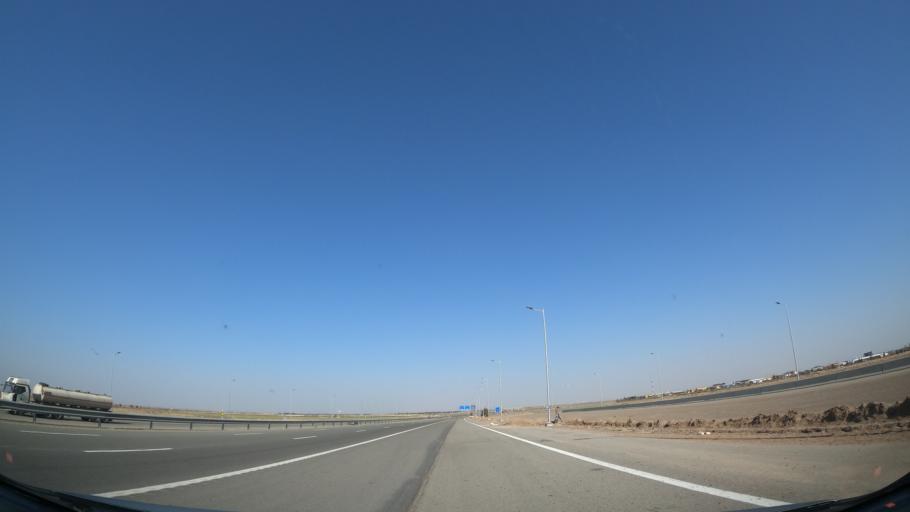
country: IR
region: Tehran
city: Eqbaliyeh
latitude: 35.1378
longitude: 51.5235
